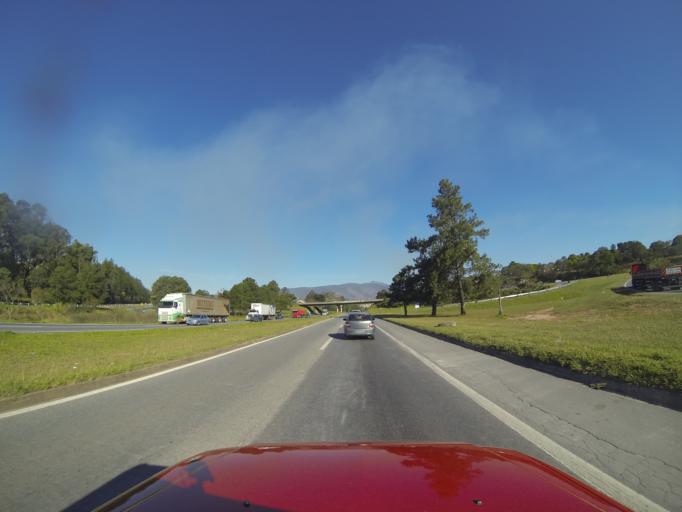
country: BR
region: Sao Paulo
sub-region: Atibaia
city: Atibaia
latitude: -23.0986
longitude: -46.5707
